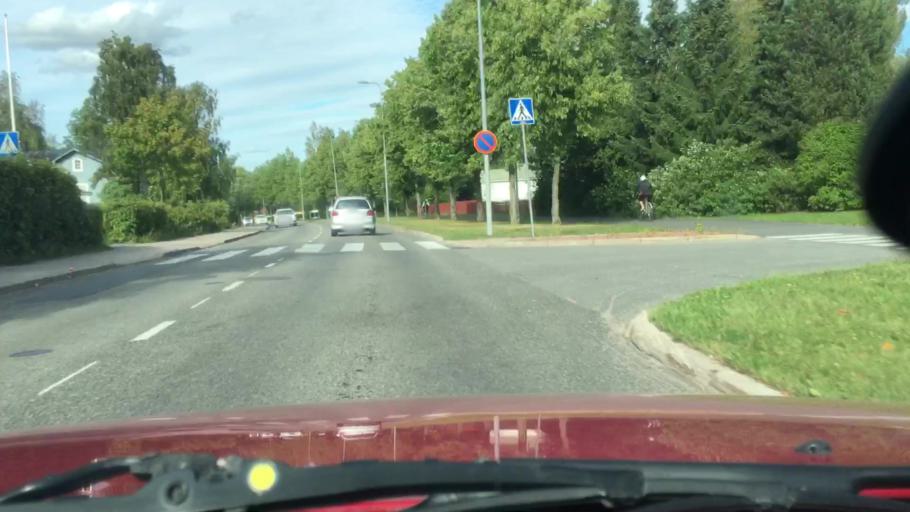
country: FI
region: Varsinais-Suomi
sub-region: Turku
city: Turku
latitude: 60.4561
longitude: 22.2443
